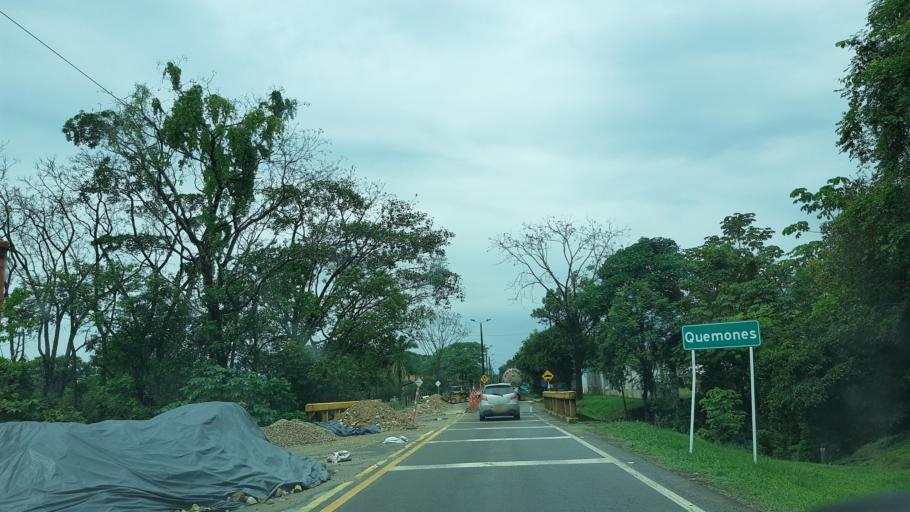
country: CO
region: Casanare
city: Monterrey
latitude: 4.8392
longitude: -72.9549
